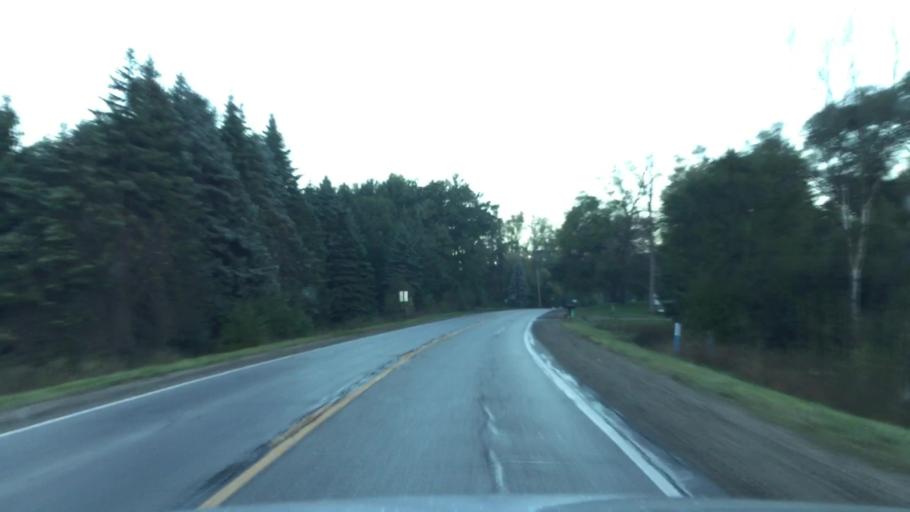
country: US
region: Michigan
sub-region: Livingston County
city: Howell
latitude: 42.6276
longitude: -83.9288
